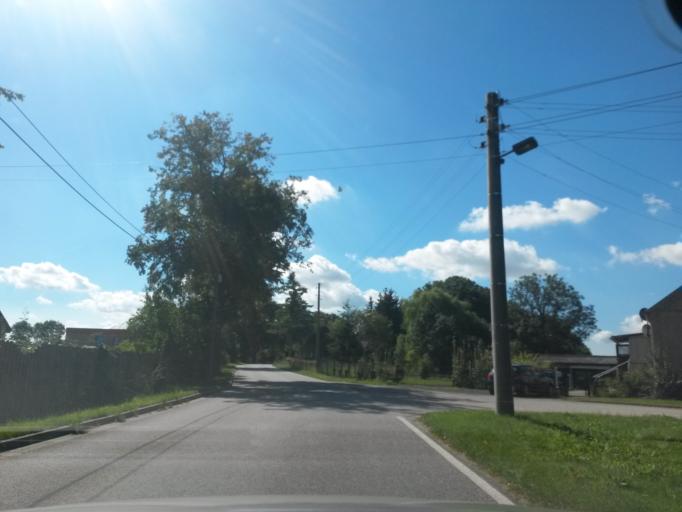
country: DE
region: Brandenburg
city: Angermunde
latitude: 53.0198
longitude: 14.0352
